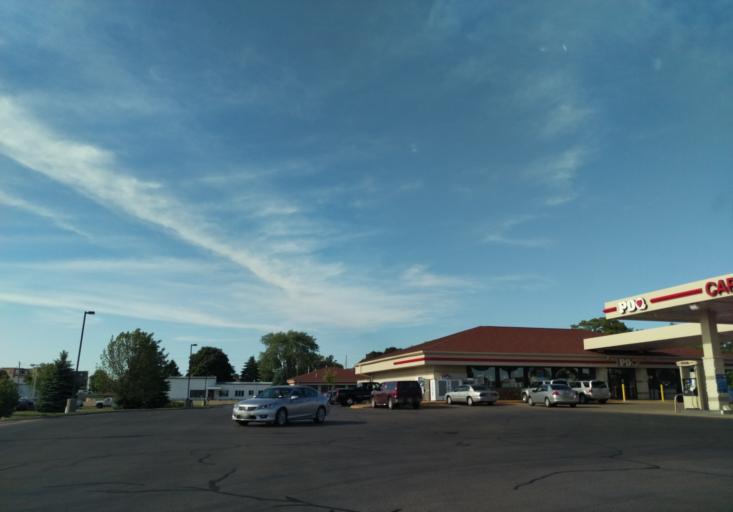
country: US
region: Wisconsin
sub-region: Dane County
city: Middleton
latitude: 43.1117
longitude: -89.5110
